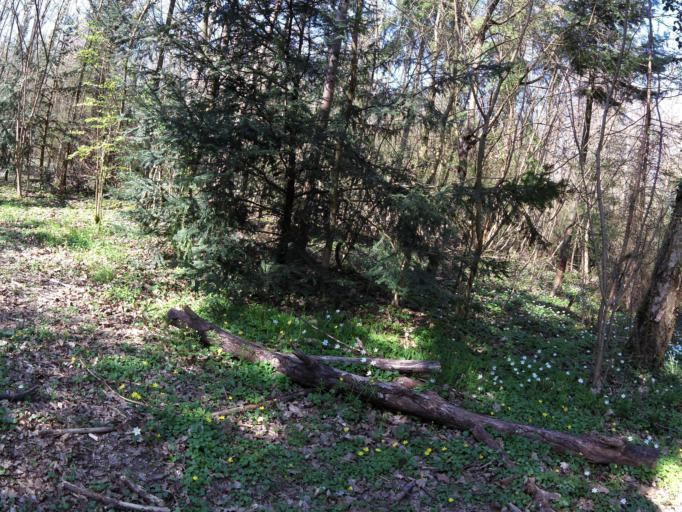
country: DE
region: Bavaria
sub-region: Regierungsbezirk Unterfranken
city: Kurnach
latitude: 49.8273
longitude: 10.0569
